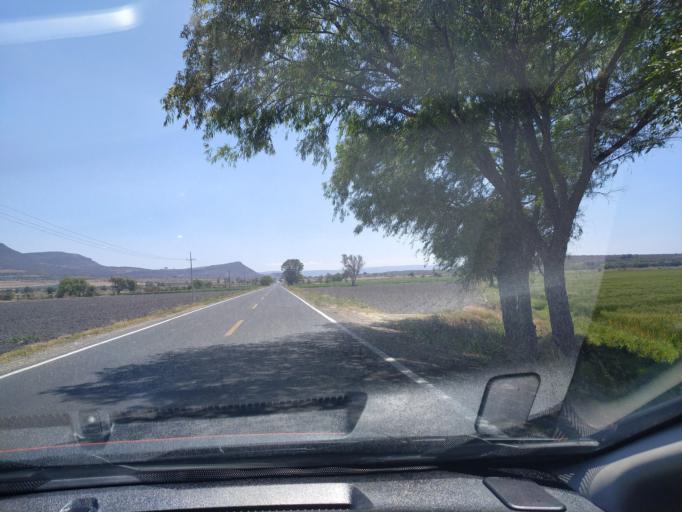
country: MX
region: Guanajuato
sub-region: San Francisco del Rincon
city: San Ignacio de Hidalgo
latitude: 20.8435
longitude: -101.8481
